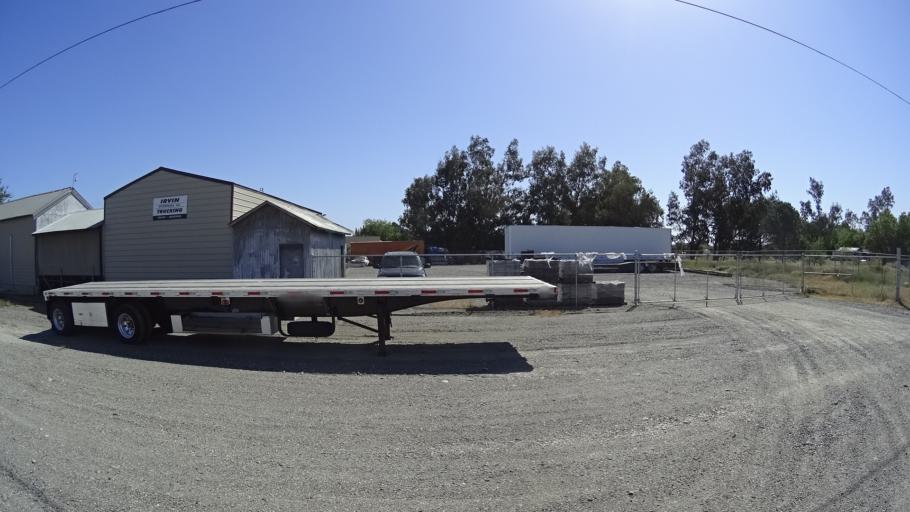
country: US
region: California
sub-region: Glenn County
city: Orland
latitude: 39.7323
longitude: -122.1962
